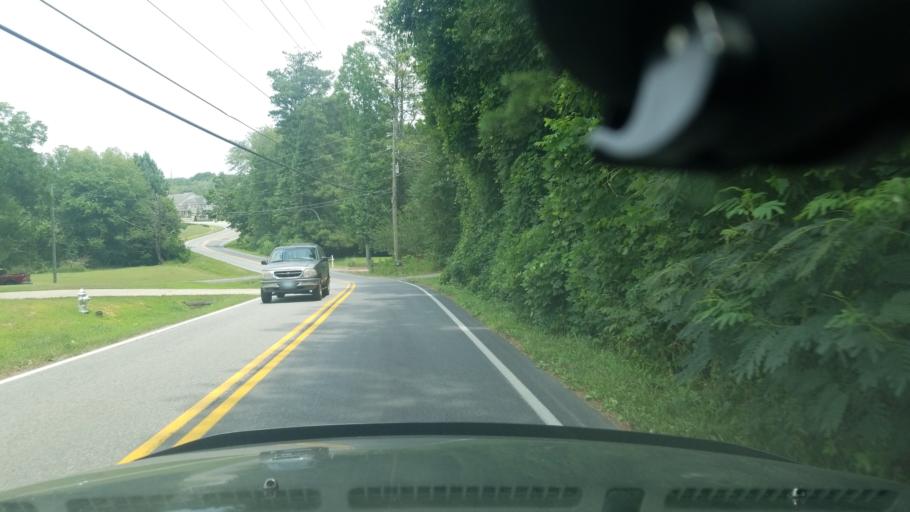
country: US
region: Georgia
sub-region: Fulton County
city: Milton
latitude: 34.1511
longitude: -84.2234
